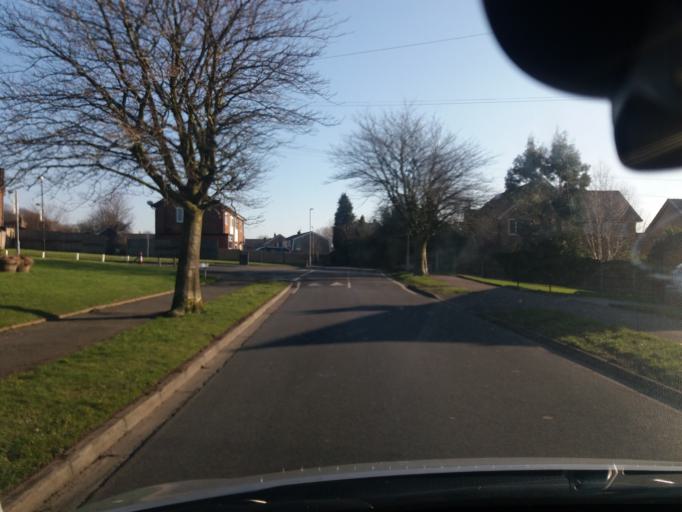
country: GB
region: England
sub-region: Lancashire
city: Adlington
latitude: 53.6174
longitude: -2.6049
